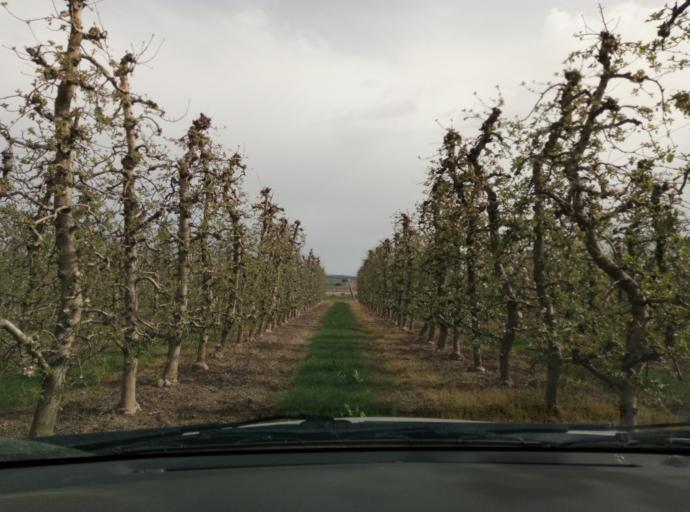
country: ES
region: Catalonia
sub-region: Provincia de Lleida
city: Tornabous
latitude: 41.7185
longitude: 1.0442
